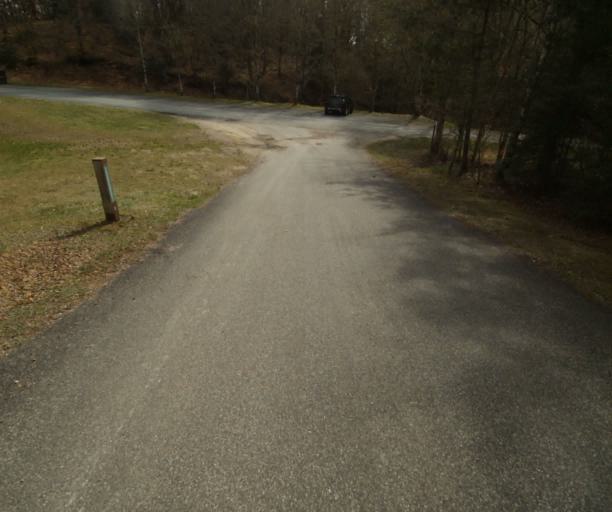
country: FR
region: Limousin
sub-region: Departement de la Correze
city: Correze
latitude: 45.2912
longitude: 1.9527
